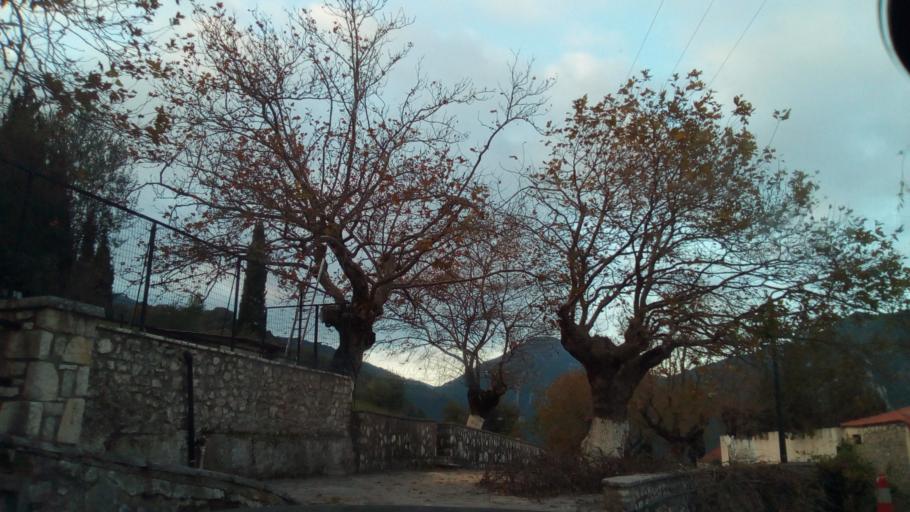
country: GR
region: West Greece
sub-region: Nomos Aitolias kai Akarnanias
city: Nafpaktos
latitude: 38.4340
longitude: 21.8206
